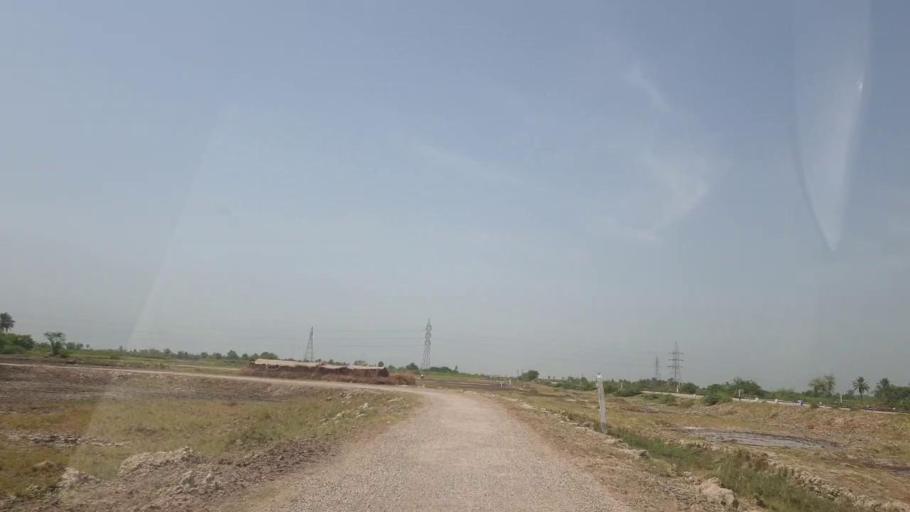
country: PK
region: Sindh
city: Gambat
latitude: 27.3169
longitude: 68.5349
